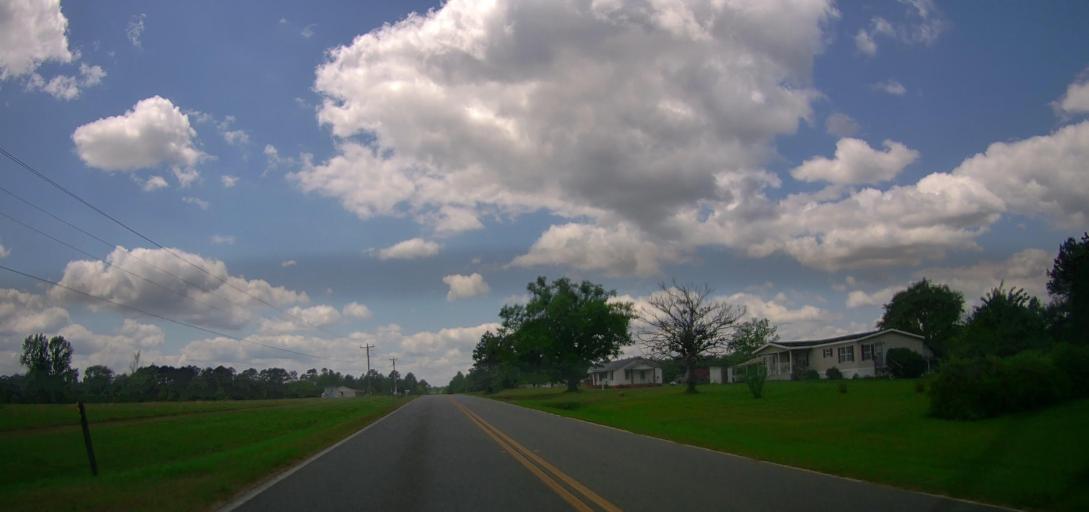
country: US
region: Georgia
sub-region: Laurens County
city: East Dublin
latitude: 32.5183
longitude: -82.7841
